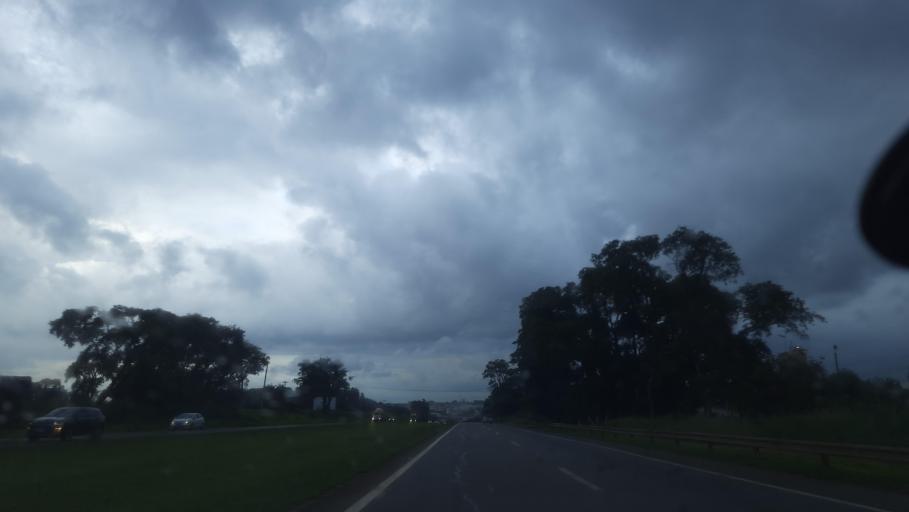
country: BR
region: Sao Paulo
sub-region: Moji-Guacu
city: Mogi-Gaucu
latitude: -22.3822
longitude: -46.9714
